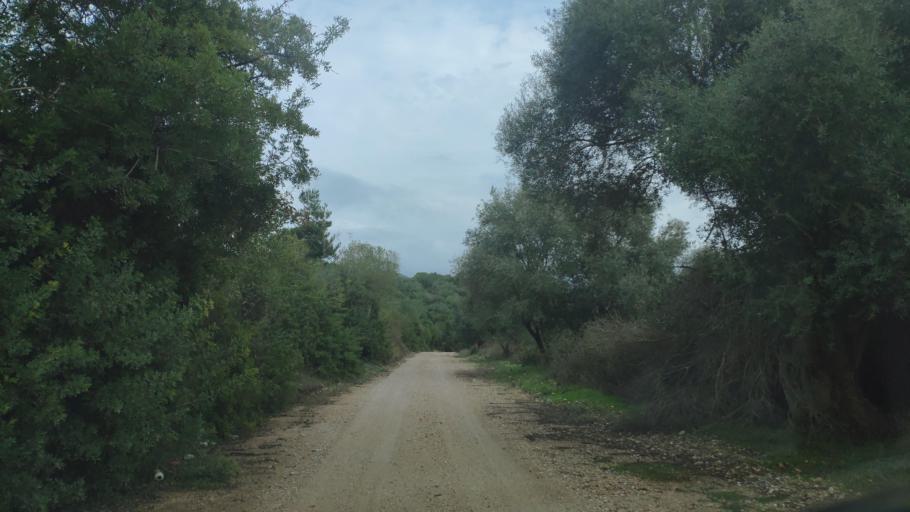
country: GR
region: West Greece
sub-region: Nomos Aitolias kai Akarnanias
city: Vonitsa
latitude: 38.9245
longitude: 20.8640
